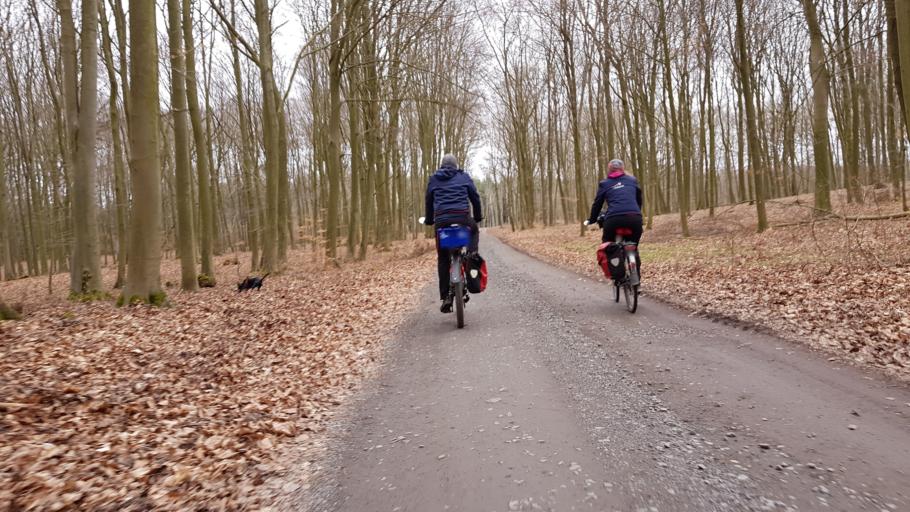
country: PL
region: West Pomeranian Voivodeship
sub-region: Powiat gryfinski
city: Banie
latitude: 53.0703
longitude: 14.7365
